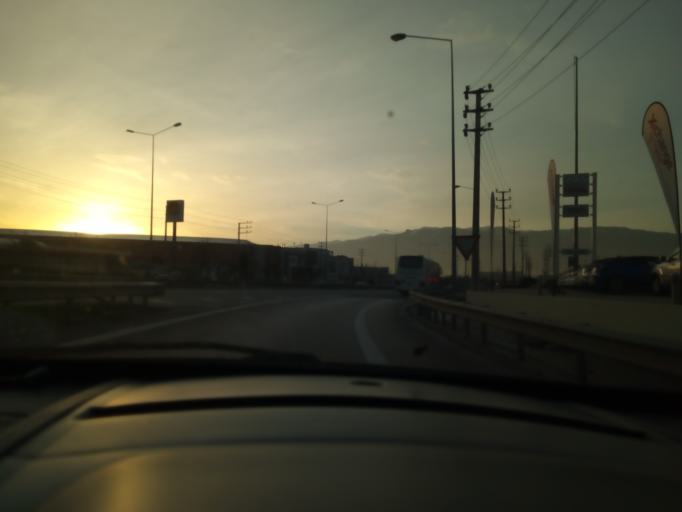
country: TR
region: Bursa
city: Demirtas
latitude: 40.2740
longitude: 29.0533
